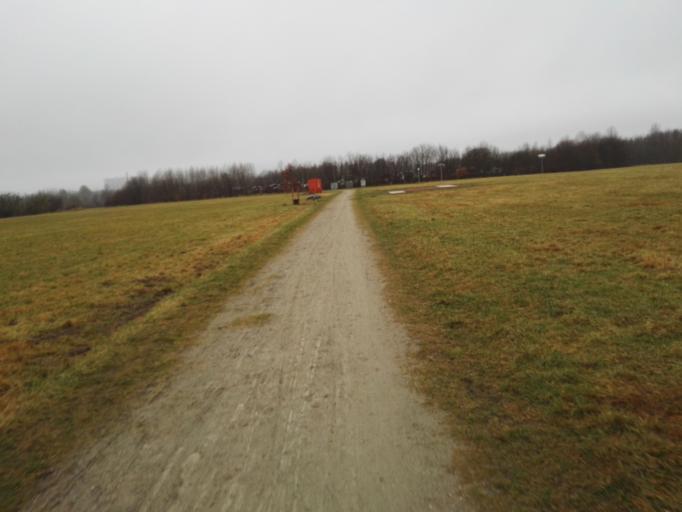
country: DK
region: Capital Region
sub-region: Ballerup Kommune
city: Ballerup
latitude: 55.7182
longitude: 12.3829
